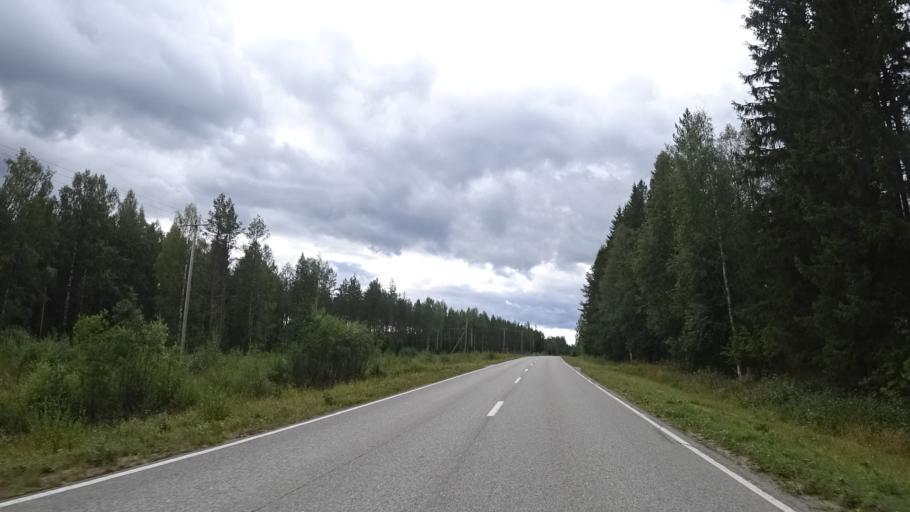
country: FI
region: North Karelia
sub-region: Joensuu
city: Ilomantsi
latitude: 62.6346
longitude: 31.2806
